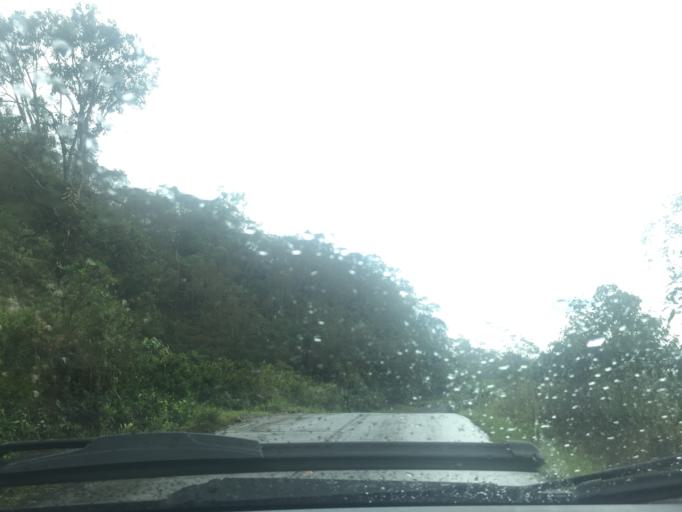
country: CO
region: Cundinamarca
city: Supata
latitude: 5.0315
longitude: -74.2478
